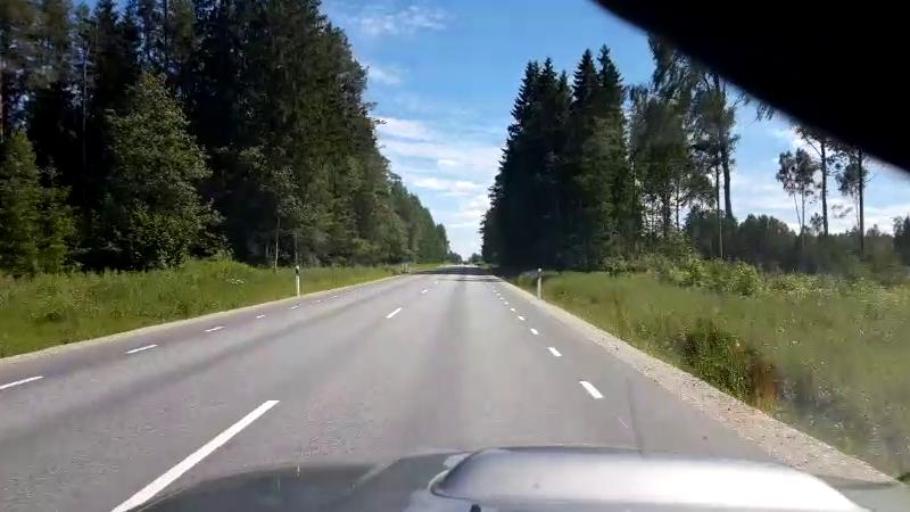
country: EE
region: Jogevamaa
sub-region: Jogeva linn
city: Jogeva
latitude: 58.7829
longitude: 26.3173
